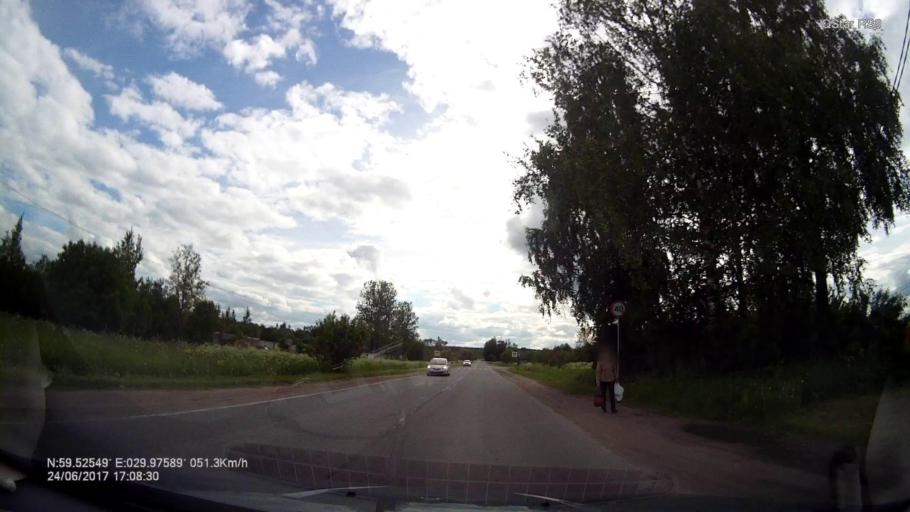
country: RU
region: Leningrad
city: Voyskovitsy
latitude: 59.5253
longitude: 29.9754
